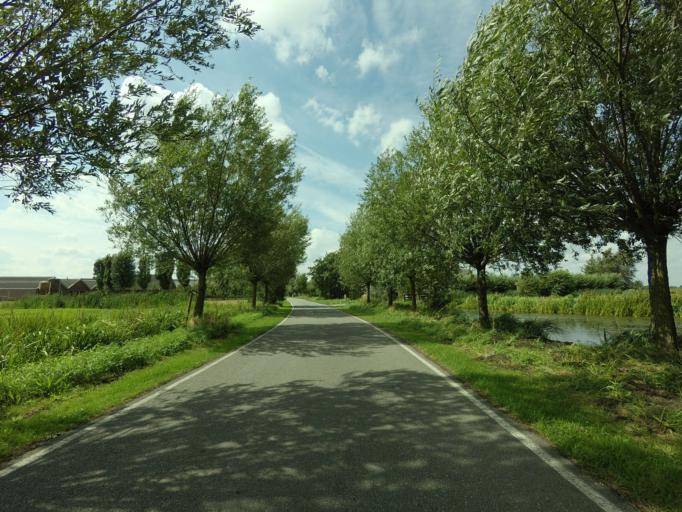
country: NL
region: Utrecht
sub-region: Gemeente Woerden
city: Woerden
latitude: 52.1273
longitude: 4.8412
